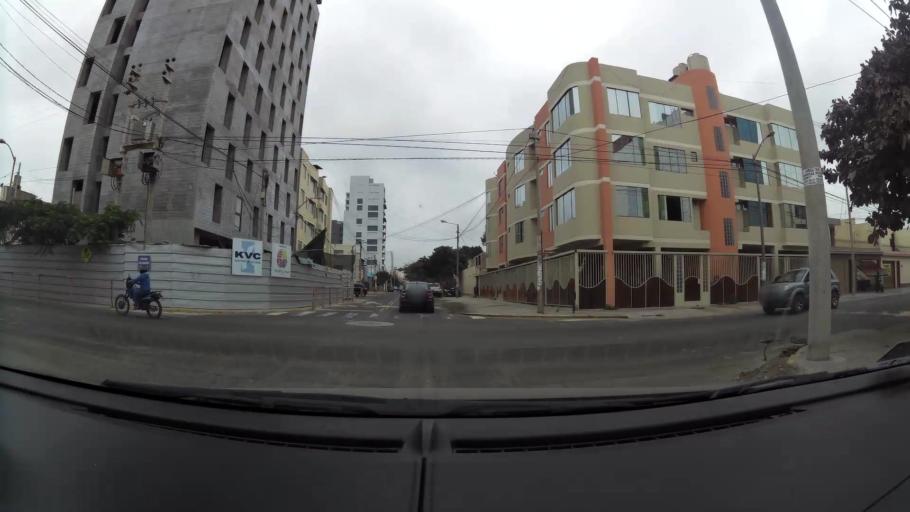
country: PE
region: La Libertad
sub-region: Provincia de Trujillo
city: Trujillo
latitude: -8.1200
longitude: -79.0370
